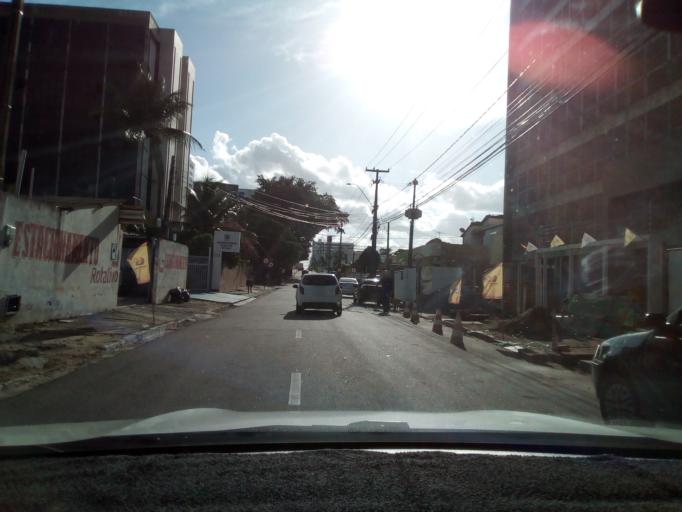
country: BR
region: Paraiba
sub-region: Joao Pessoa
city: Joao Pessoa
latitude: -7.1186
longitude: -34.8562
